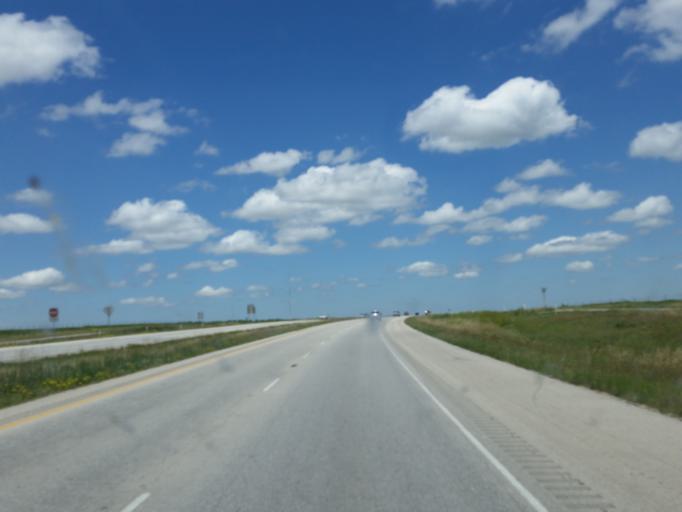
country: US
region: Texas
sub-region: Nolan County
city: Sweetwater
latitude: 32.4655
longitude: -100.3817
